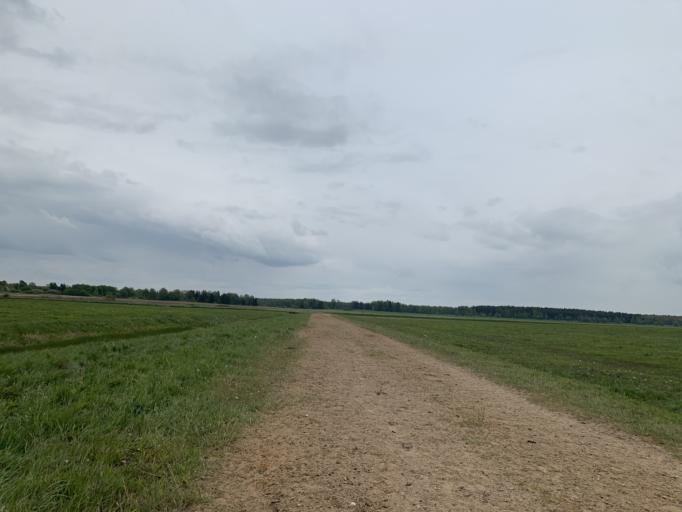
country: BY
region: Minsk
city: Kapyl'
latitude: 53.2480
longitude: 26.9459
